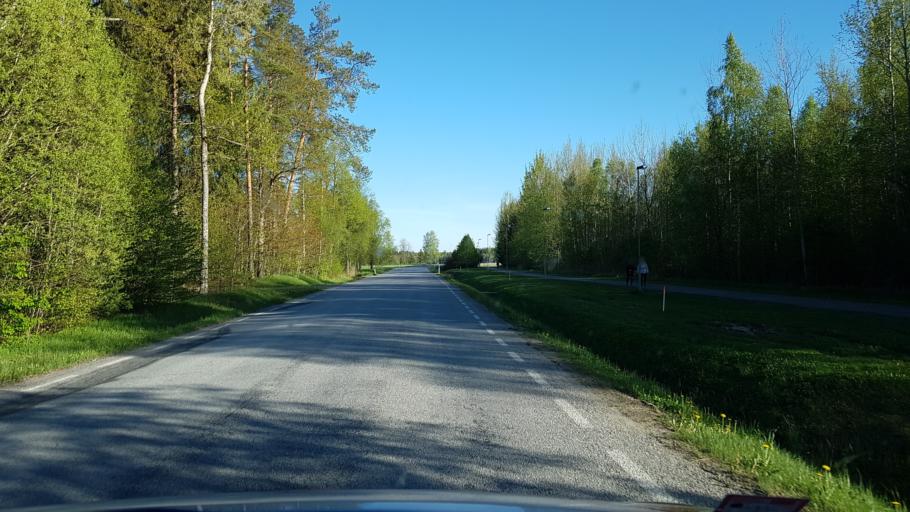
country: EE
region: Vorumaa
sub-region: Voru linn
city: Voru
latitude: 57.8933
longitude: 27.0012
